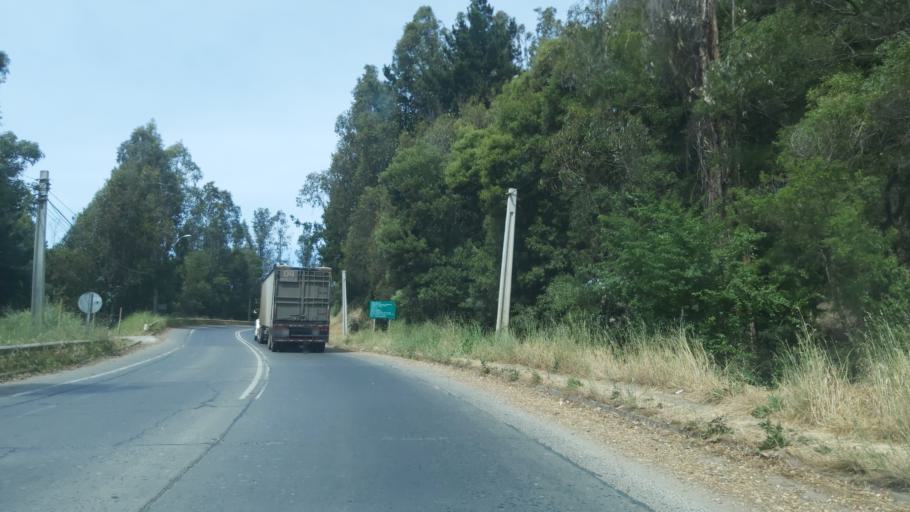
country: CL
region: Maule
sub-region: Provincia de Talca
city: Constitucion
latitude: -35.3463
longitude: -72.4159
